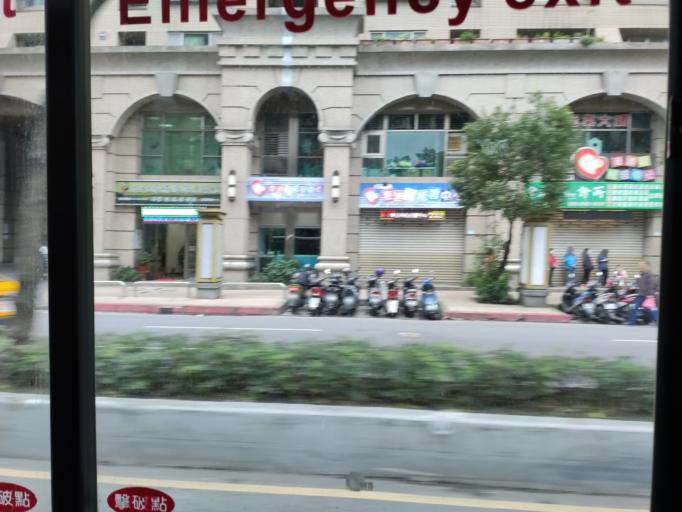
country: TW
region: Taipei
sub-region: Taipei
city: Banqiao
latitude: 25.0055
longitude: 121.4781
